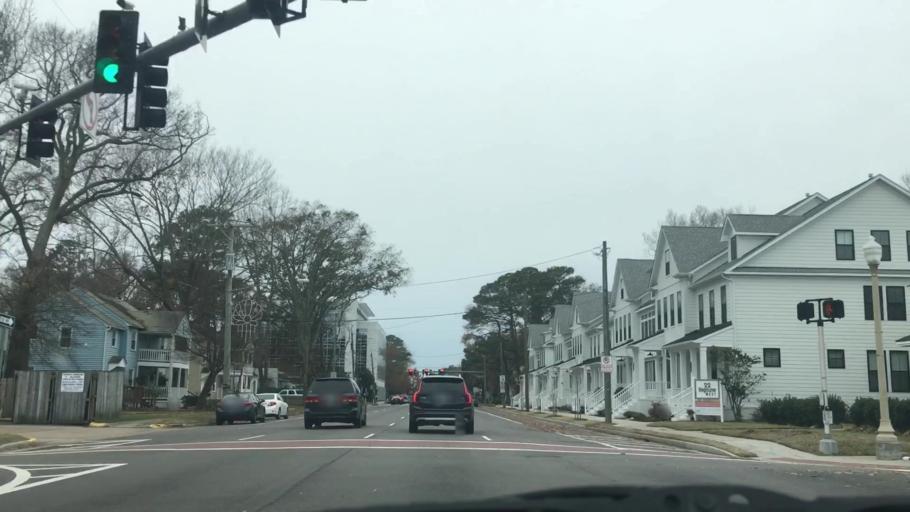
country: US
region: Virginia
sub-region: City of Virginia Beach
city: Virginia Beach
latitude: 36.8494
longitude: -75.9805
